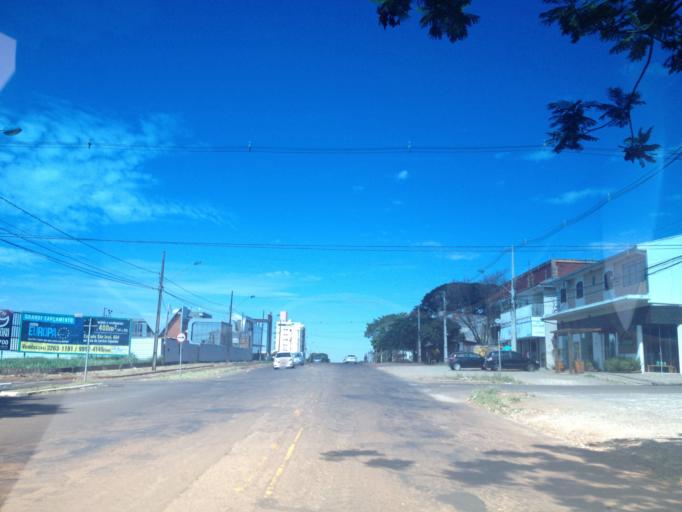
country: BR
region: Parana
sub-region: Maringa
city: Maringa
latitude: -23.4437
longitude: -51.9553
